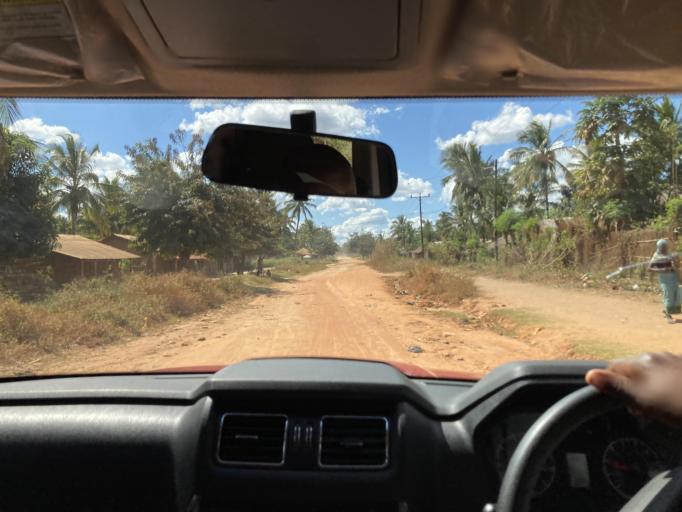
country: MZ
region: Cabo Delgado
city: Montepuez
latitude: -13.1446
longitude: 38.9931
